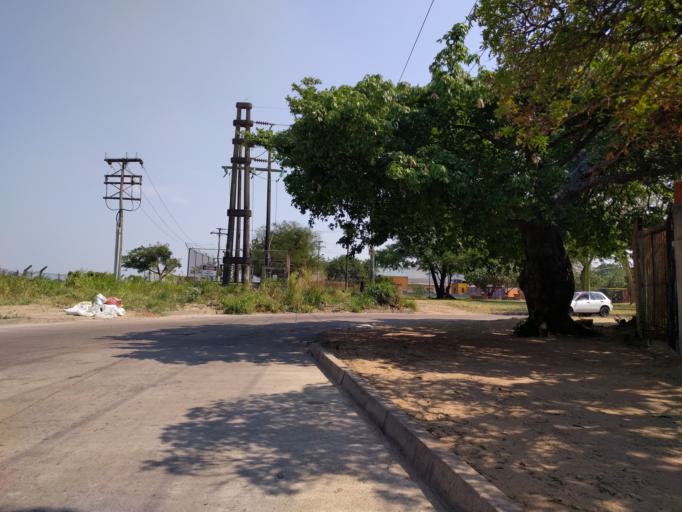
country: BO
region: Santa Cruz
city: Santa Cruz de la Sierra
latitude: -17.8081
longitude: -63.1727
